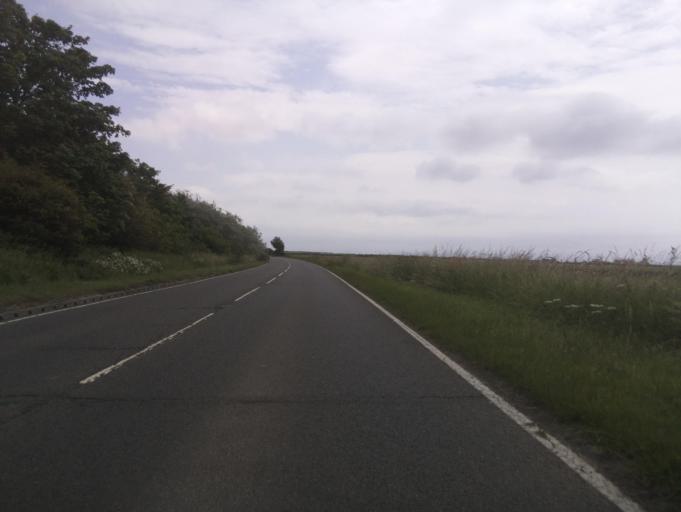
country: GB
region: Wales
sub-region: Vale of Glamorgan
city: Llantwit Major
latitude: 51.4030
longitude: -3.4523
